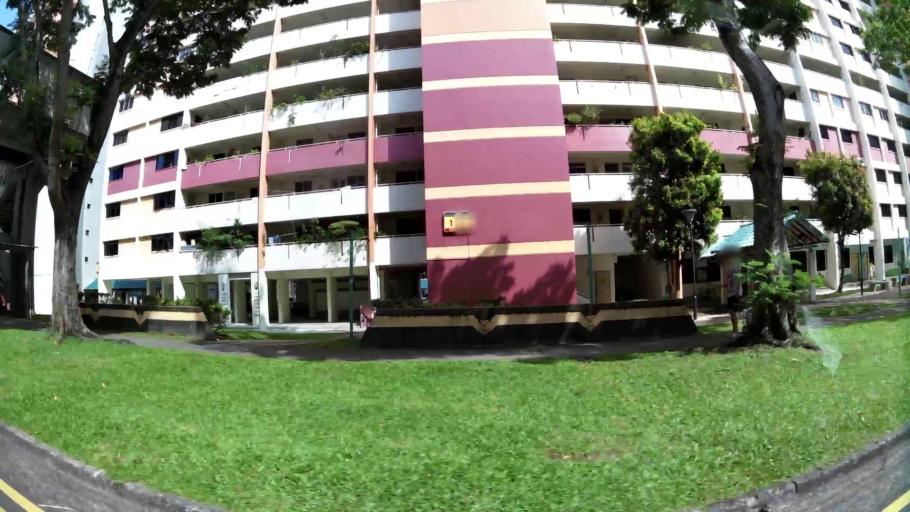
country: SG
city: Singapore
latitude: 1.3520
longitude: 103.8864
